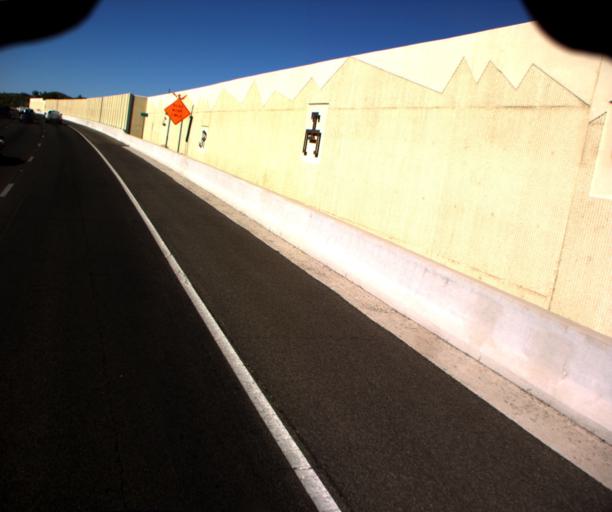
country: US
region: Arizona
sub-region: Pima County
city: Oro Valley
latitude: 32.4121
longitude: -110.9391
